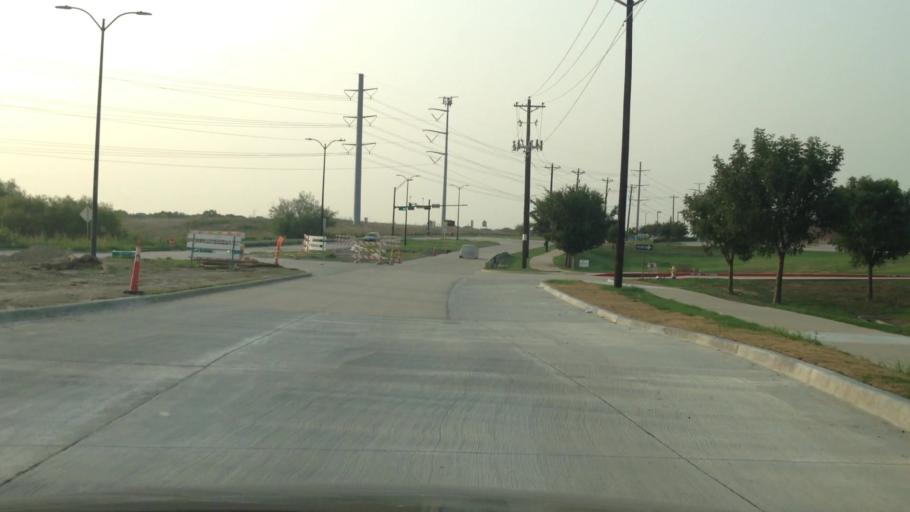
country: US
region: Texas
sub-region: Collin County
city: Frisco
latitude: 33.1236
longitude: -96.8471
